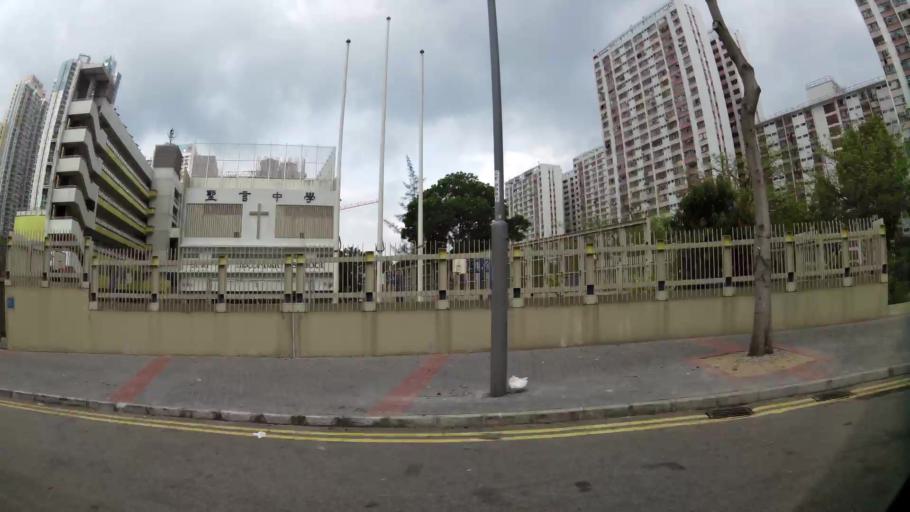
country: HK
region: Kowloon City
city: Kowloon
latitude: 22.3322
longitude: 114.2161
